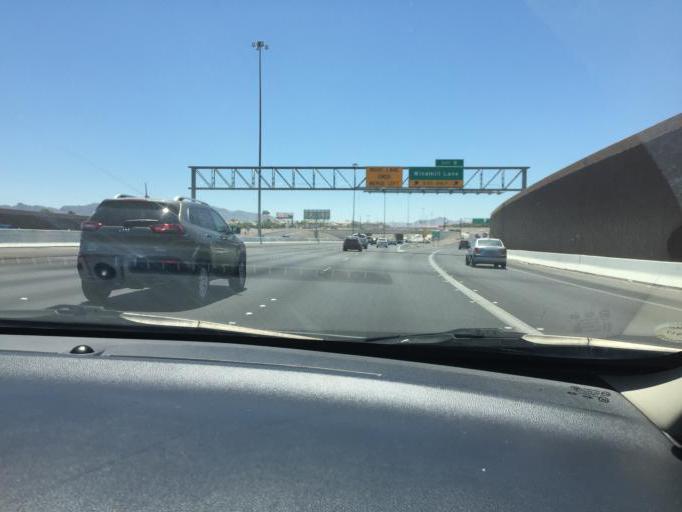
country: US
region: Nevada
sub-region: Clark County
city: Paradise
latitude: 36.0465
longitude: -115.1347
